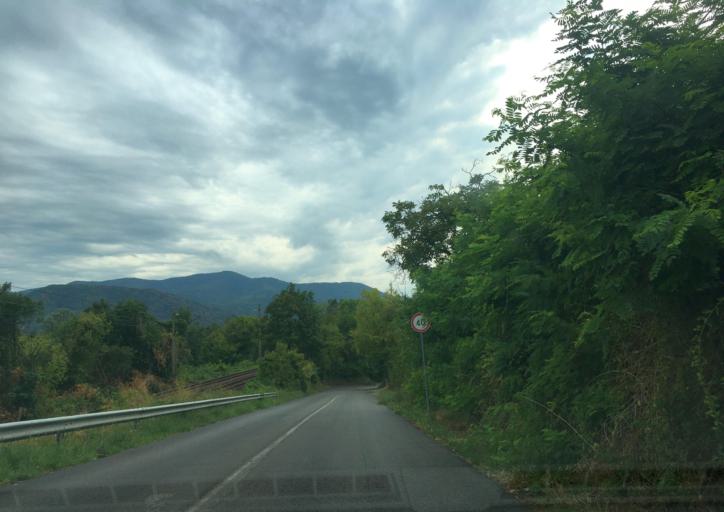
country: HU
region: Pest
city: Nagymaros
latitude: 47.7747
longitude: 18.9472
